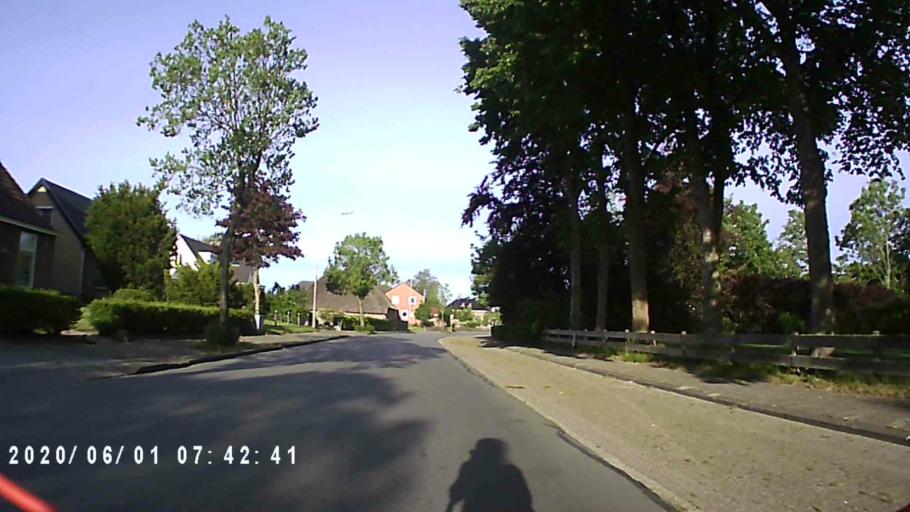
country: NL
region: Friesland
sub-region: Gemeente Dantumadiel
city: Damwald
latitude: 53.2910
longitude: 5.9773
